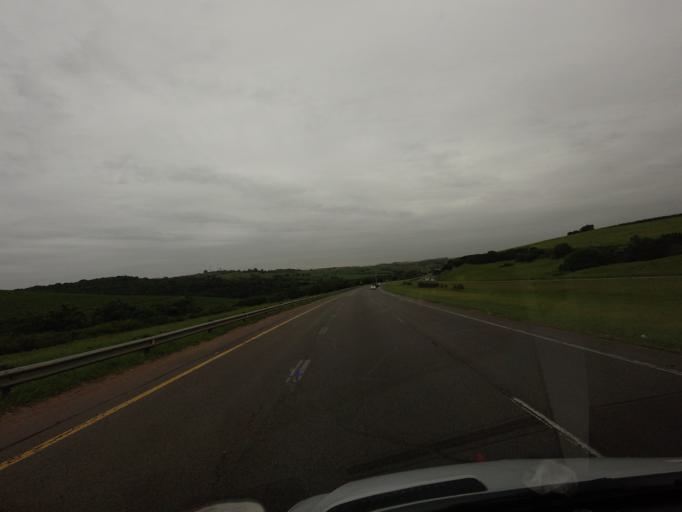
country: ZA
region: KwaZulu-Natal
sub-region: eThekwini Metropolitan Municipality
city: Durban
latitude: -29.6887
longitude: 31.0857
